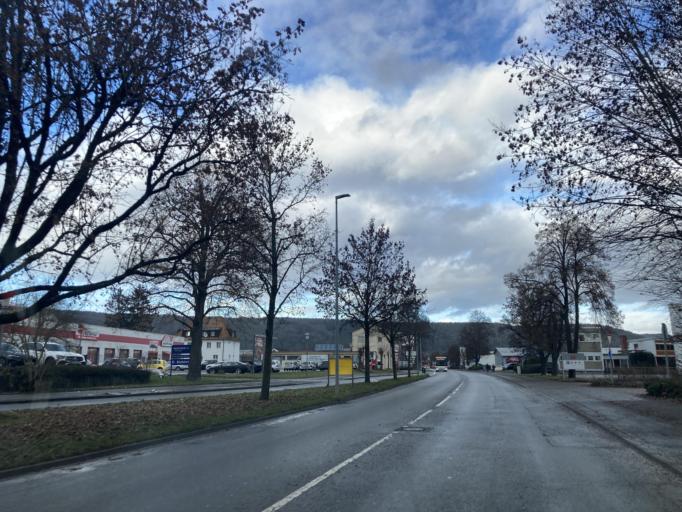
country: DE
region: Baden-Wuerttemberg
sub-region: Freiburg Region
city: Tuttlingen
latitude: 47.9937
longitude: 8.8281
